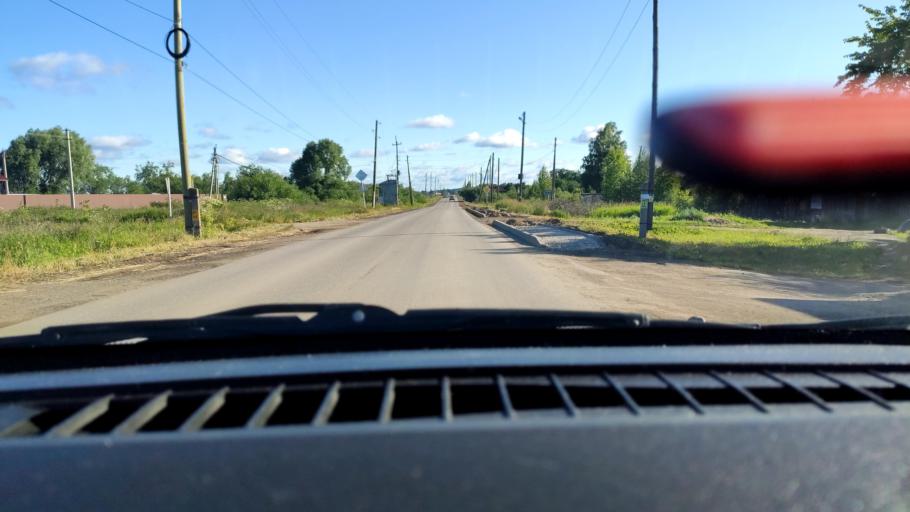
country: RU
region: Perm
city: Kultayevo
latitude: 57.8722
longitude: 55.9184
